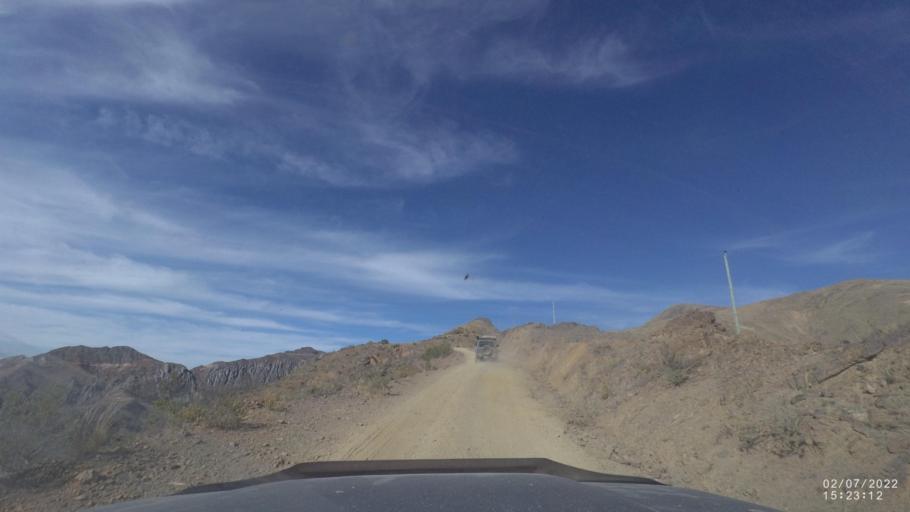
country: BO
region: Cochabamba
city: Irpa Irpa
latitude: -17.8735
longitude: -66.4207
